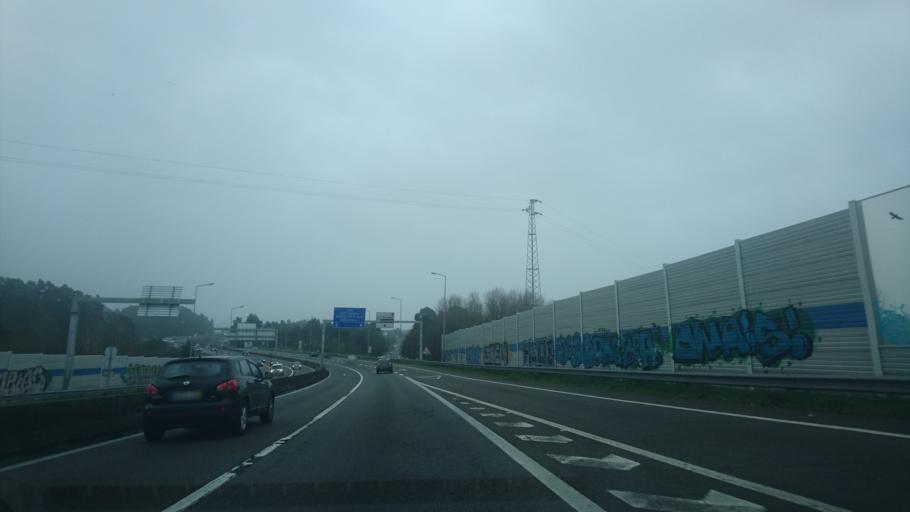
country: PT
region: Porto
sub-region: Vila Nova de Gaia
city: Gulpilhares
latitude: 41.0911
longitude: -8.6306
